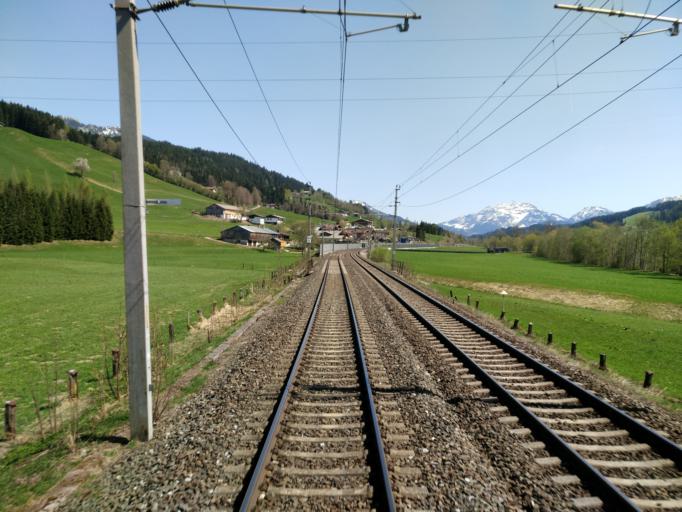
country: AT
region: Tyrol
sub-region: Politischer Bezirk Kitzbuhel
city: Sankt Johann in Tirol
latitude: 47.5105
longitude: 12.4641
